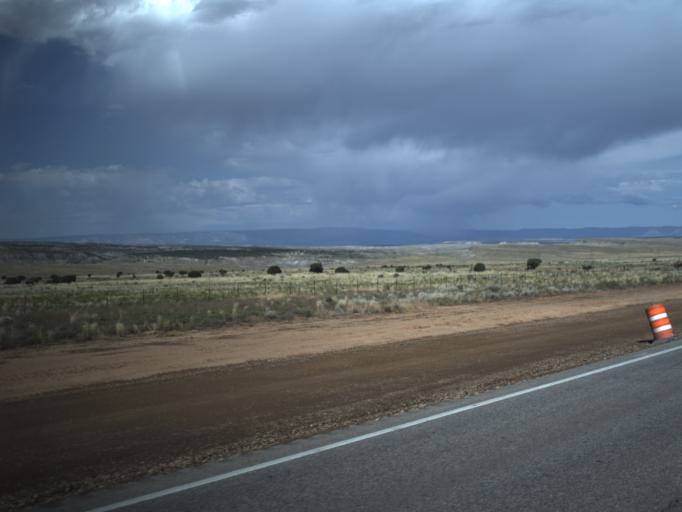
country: US
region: Utah
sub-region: Carbon County
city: East Carbon City
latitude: 39.4271
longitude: -110.4480
